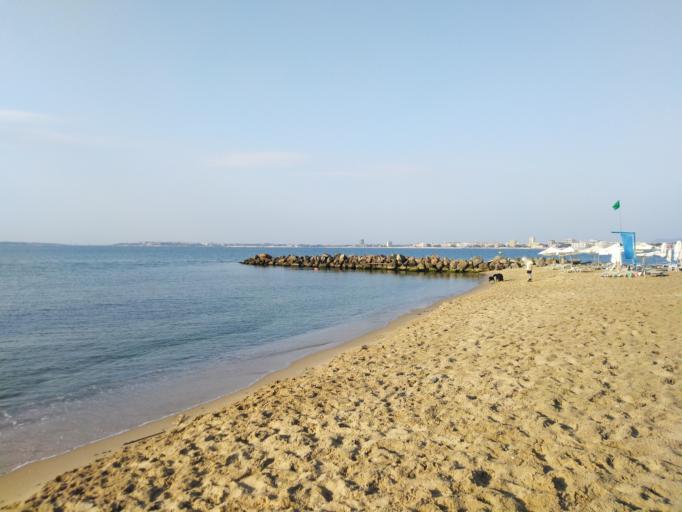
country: BG
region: Burgas
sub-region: Obshtina Nesebur
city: Sveti Vlas
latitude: 42.7075
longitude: 27.7407
